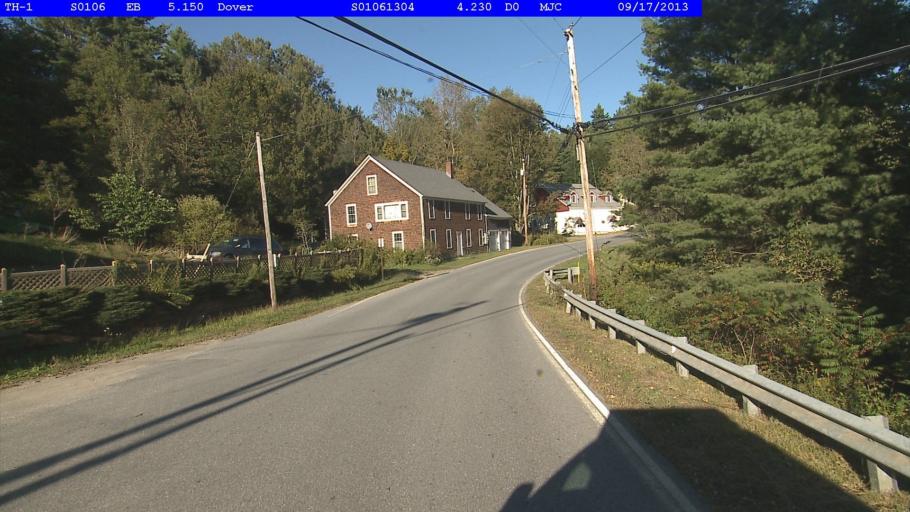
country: US
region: Vermont
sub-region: Windham County
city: Dover
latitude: 42.9509
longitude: -72.7683
